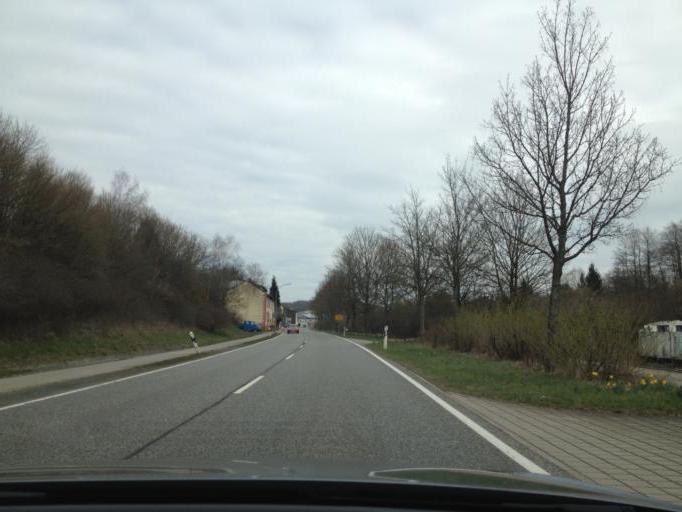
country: DE
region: Rheinland-Pfalz
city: Hahnweiler
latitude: 49.5514
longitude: 7.1962
